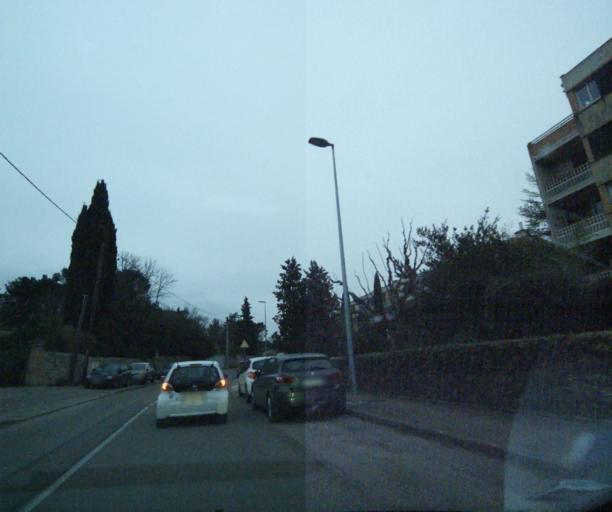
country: FR
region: Provence-Alpes-Cote d'Azur
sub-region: Departement des Bouches-du-Rhone
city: Aix-en-Provence
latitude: 43.5238
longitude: 5.4679
